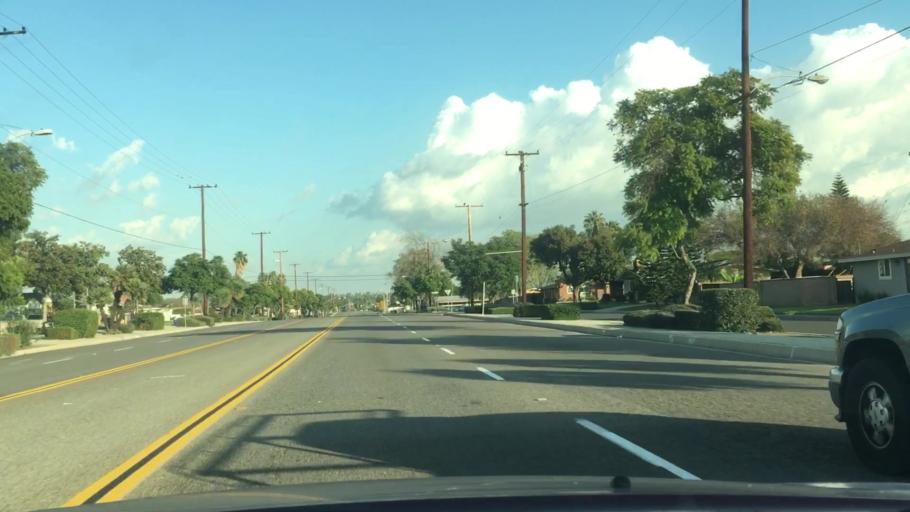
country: US
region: California
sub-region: Orange County
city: Buena Park
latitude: 33.8881
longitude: -118.0070
